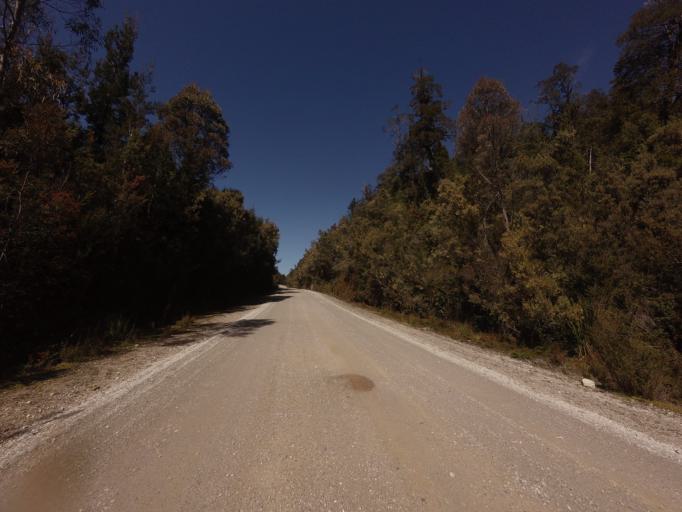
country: AU
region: Tasmania
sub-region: Huon Valley
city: Geeveston
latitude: -42.8299
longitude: 146.3859
